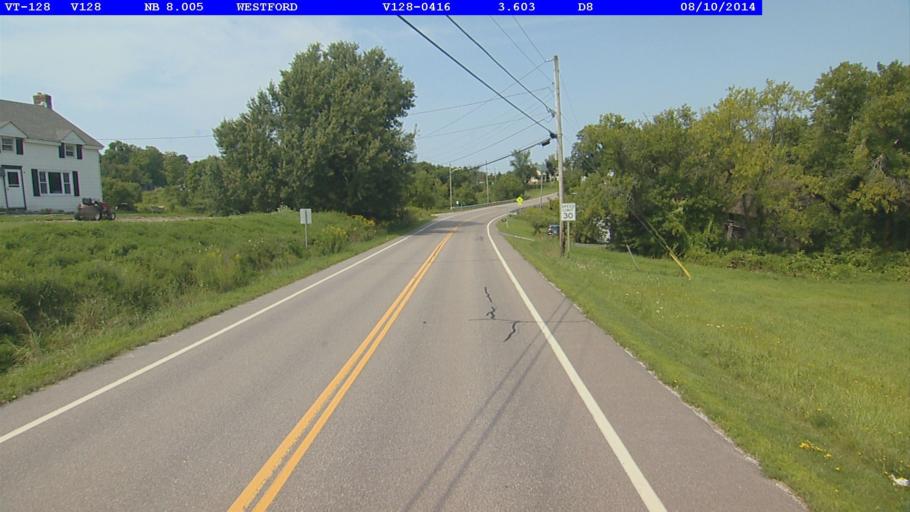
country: US
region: Vermont
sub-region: Chittenden County
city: Milton
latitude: 44.6090
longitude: -73.0093
